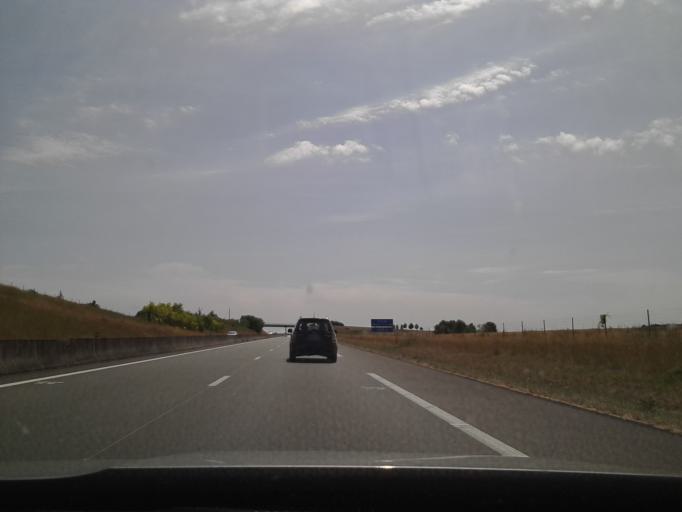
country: FR
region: Pays de la Loire
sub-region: Departement de la Sarthe
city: Chateau-du-Loir
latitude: 47.6582
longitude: 0.4376
